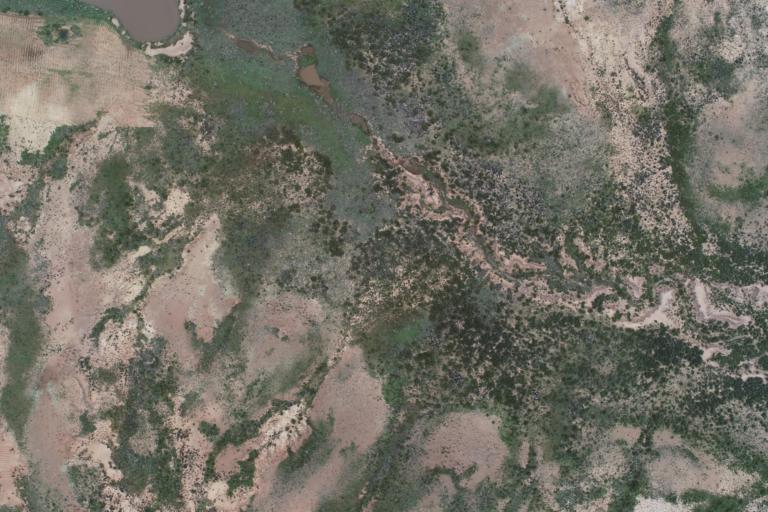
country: BO
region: La Paz
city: Curahuara de Carangas
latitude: -17.2950
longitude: -68.5091
